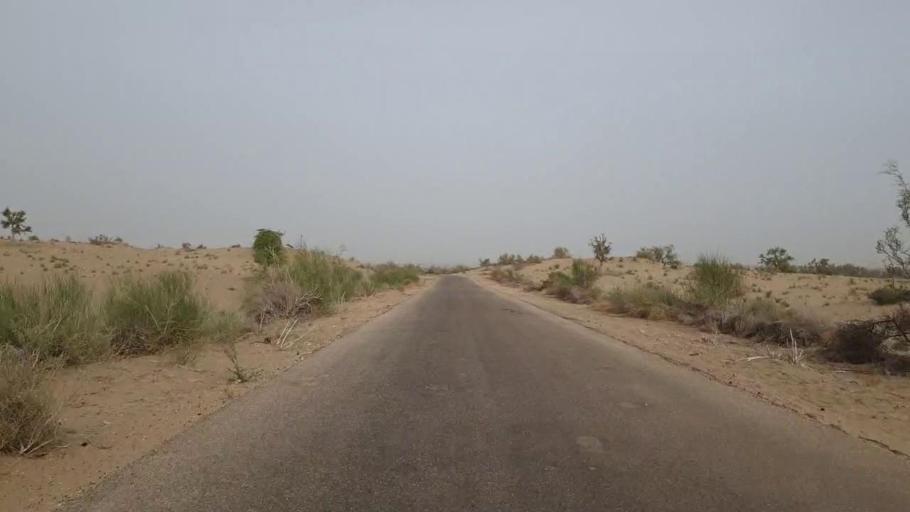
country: PK
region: Sindh
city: Islamkot
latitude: 24.5514
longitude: 70.3539
